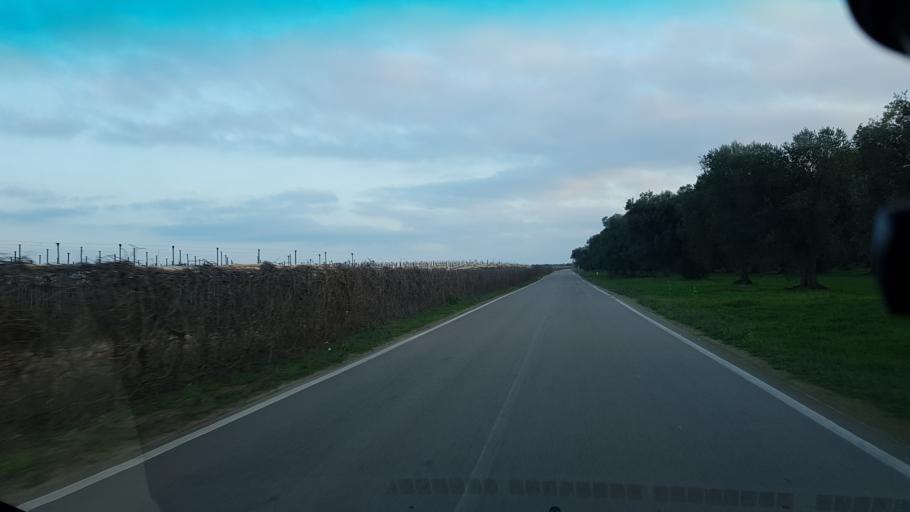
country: IT
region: Apulia
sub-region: Provincia di Brindisi
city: San Vito dei Normanni
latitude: 40.6328
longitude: 17.7822
